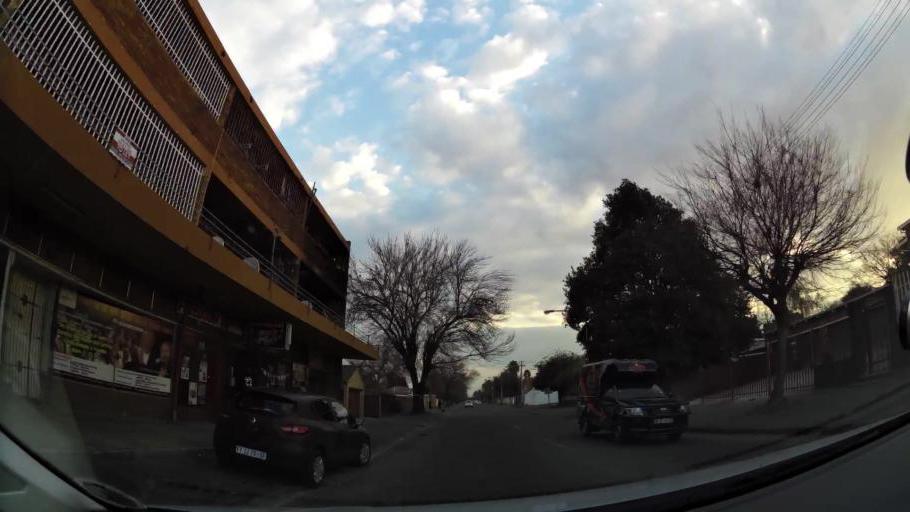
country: ZA
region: Gauteng
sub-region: Ekurhuleni Metropolitan Municipality
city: Germiston
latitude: -26.1892
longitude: 28.1552
